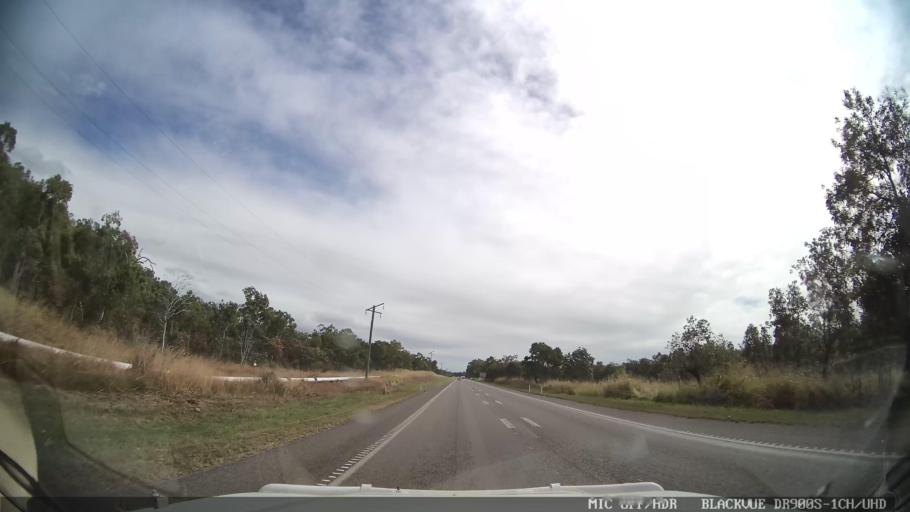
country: AU
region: Queensland
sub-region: Hinchinbrook
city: Ingham
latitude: -19.0063
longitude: 146.3603
